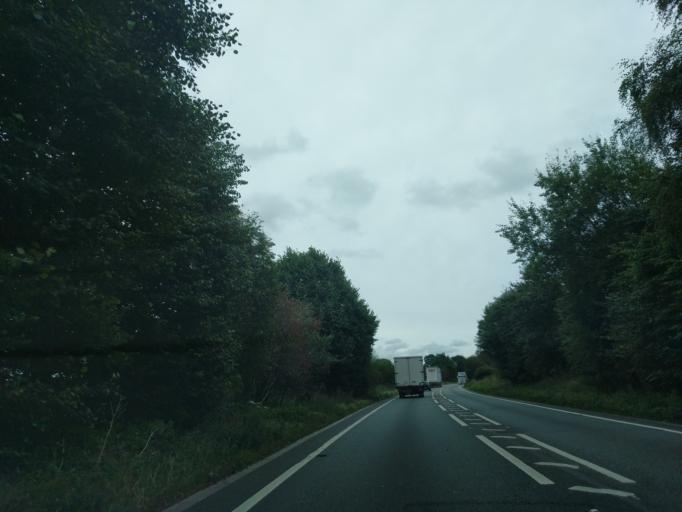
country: GB
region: England
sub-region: Cheshire East
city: Weston
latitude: 53.0732
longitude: -2.3555
